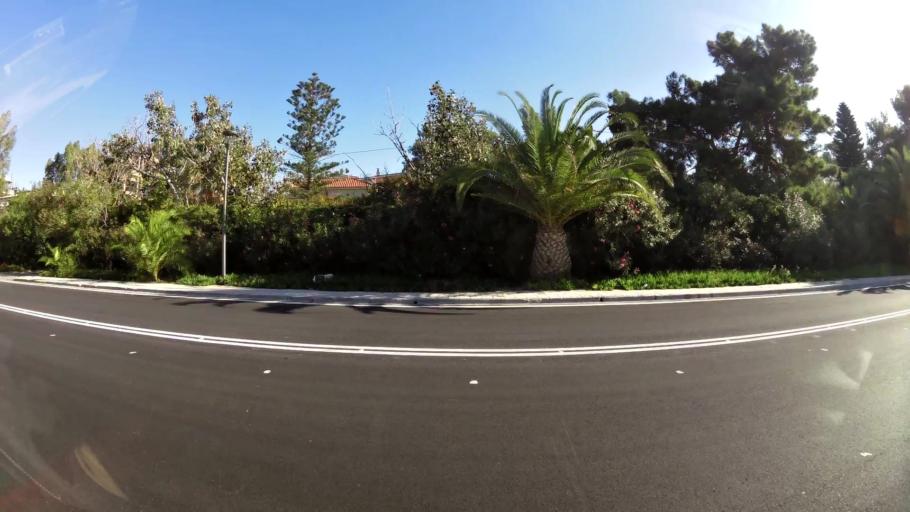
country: GR
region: Attica
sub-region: Nomarchia Athinas
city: Elliniko
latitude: 37.8728
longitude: 23.7341
